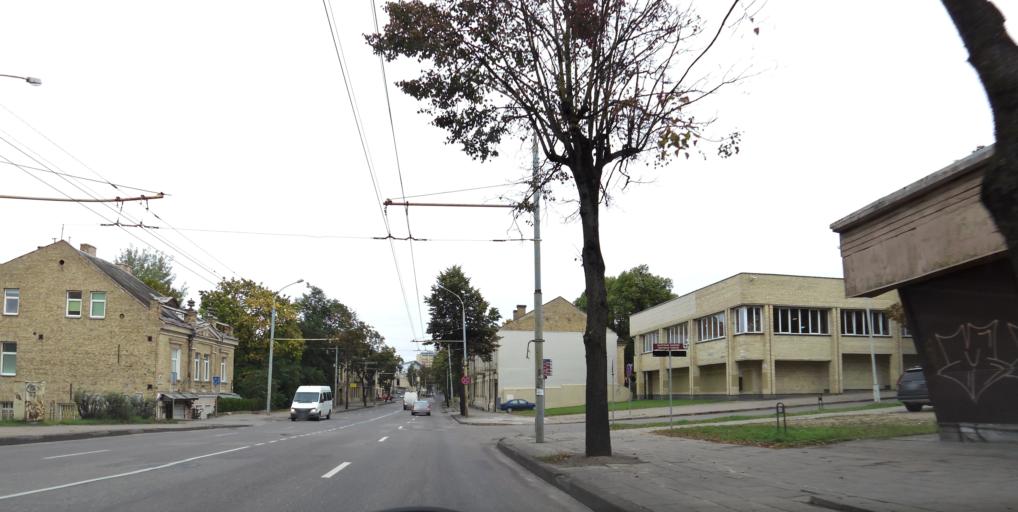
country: LT
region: Vilnius County
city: Rasos
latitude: 54.7001
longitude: 25.3090
